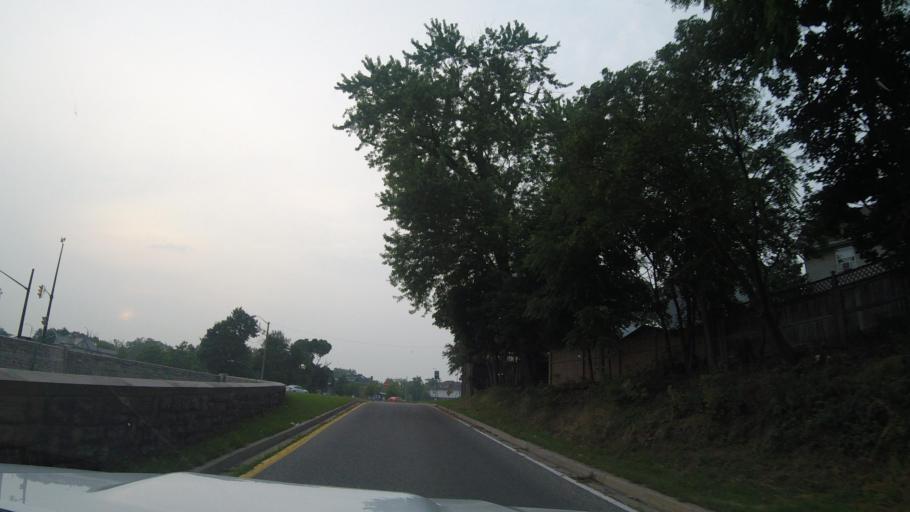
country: CA
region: Ontario
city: Niagara Falls
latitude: 43.0960
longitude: -79.0722
